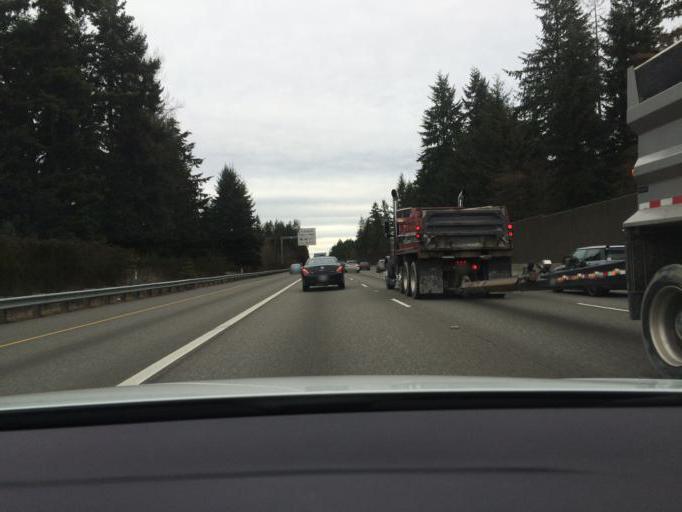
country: US
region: Washington
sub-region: Snohomish County
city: Mill Creek
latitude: 47.8874
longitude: -122.2260
